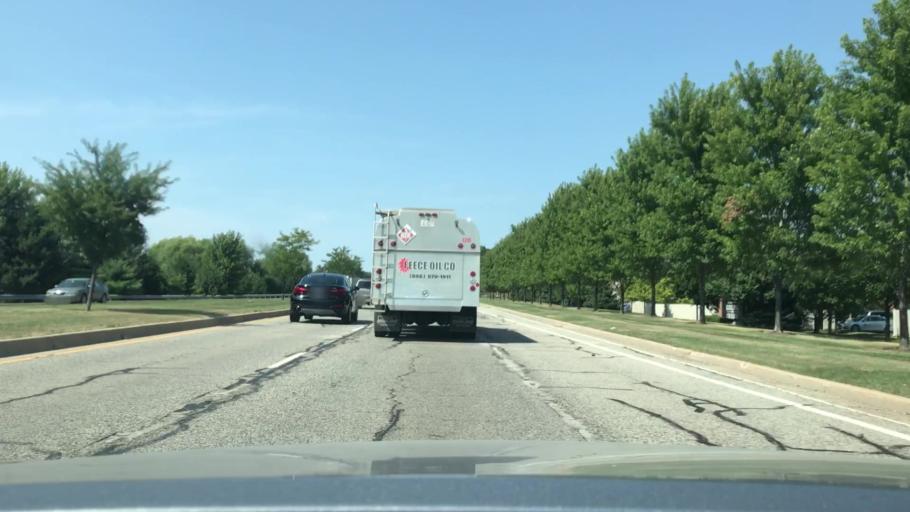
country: US
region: Illinois
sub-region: Kane County
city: Batavia
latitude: 41.8191
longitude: -88.2797
